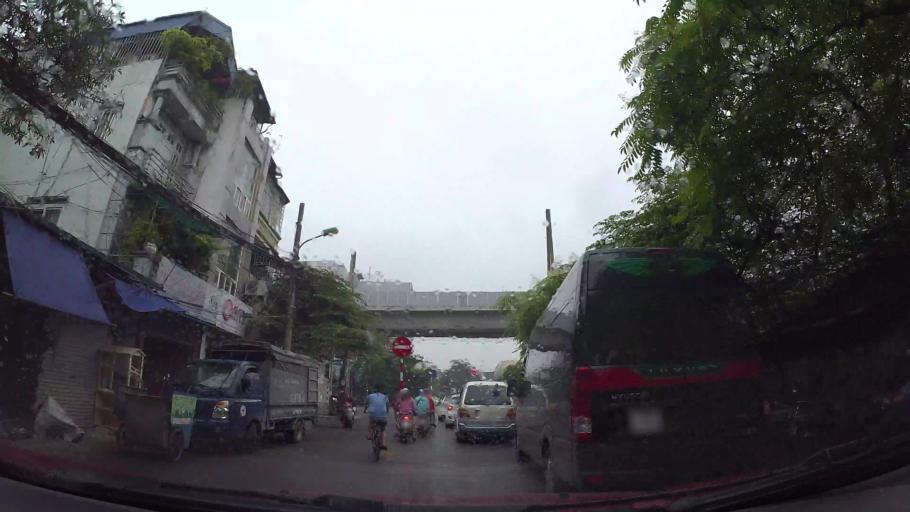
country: VN
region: Ha Noi
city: Dong Da
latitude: 21.0214
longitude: 105.8254
